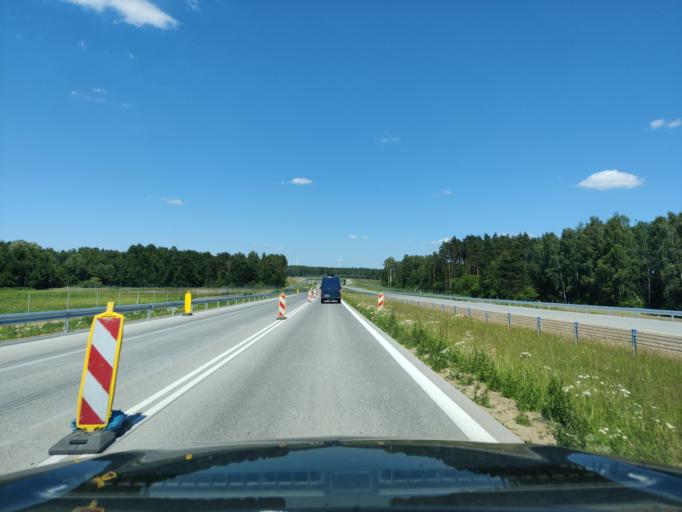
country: PL
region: Masovian Voivodeship
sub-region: Powiat mlawski
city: Mlawa
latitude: 53.1342
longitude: 20.4202
